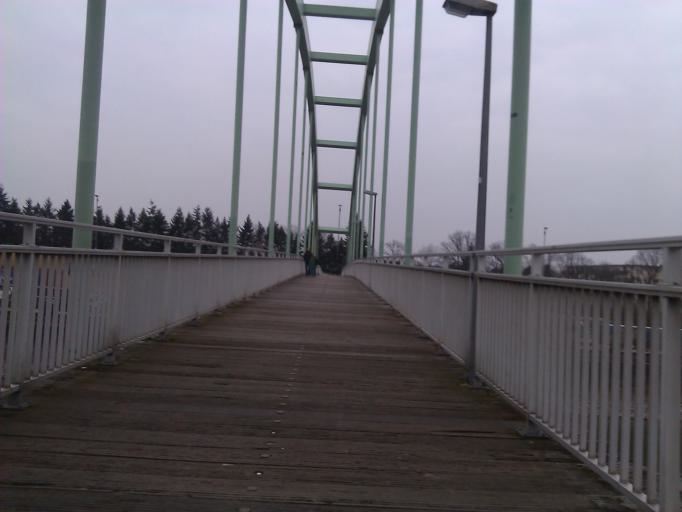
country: DE
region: North Rhine-Westphalia
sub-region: Regierungsbezirk Koln
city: Riehl
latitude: 50.9856
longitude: 6.9693
